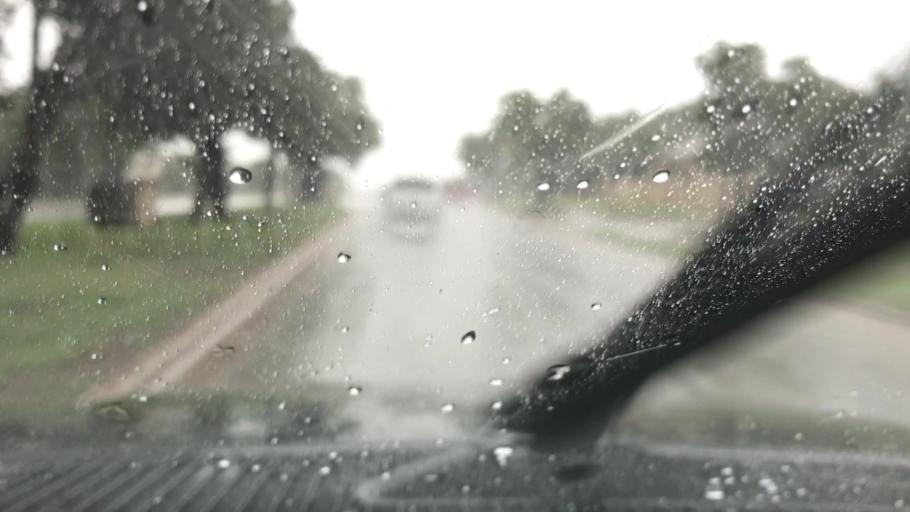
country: US
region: Texas
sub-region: Williamson County
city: Leander
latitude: 30.5331
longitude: -97.8596
